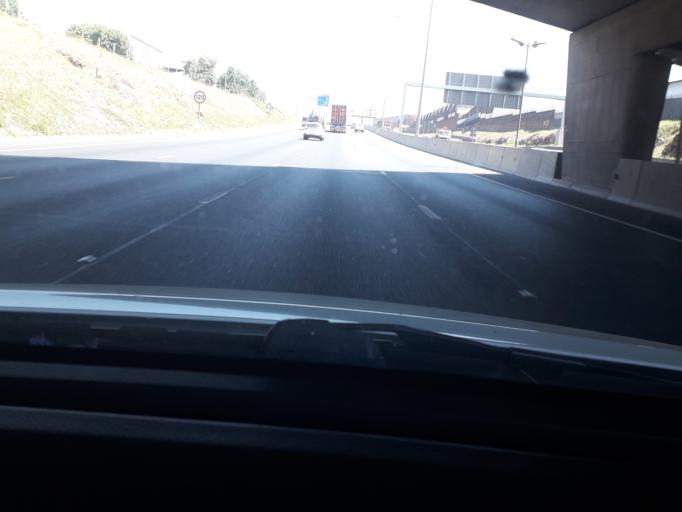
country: ZA
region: Gauteng
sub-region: Ekurhuleni Metropolitan Municipality
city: Germiston
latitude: -26.1708
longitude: 28.1921
